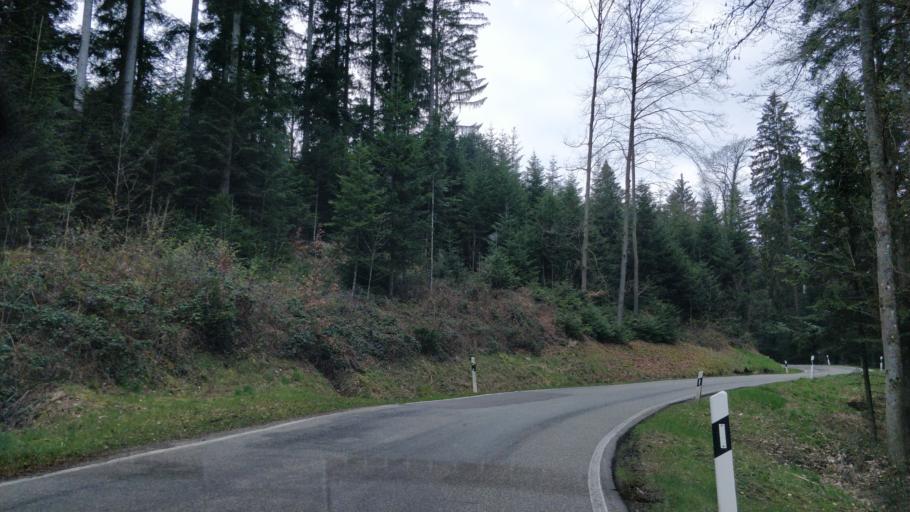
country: DE
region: Baden-Wuerttemberg
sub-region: Regierungsbezirk Stuttgart
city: Murrhardt
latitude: 48.9906
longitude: 9.5779
